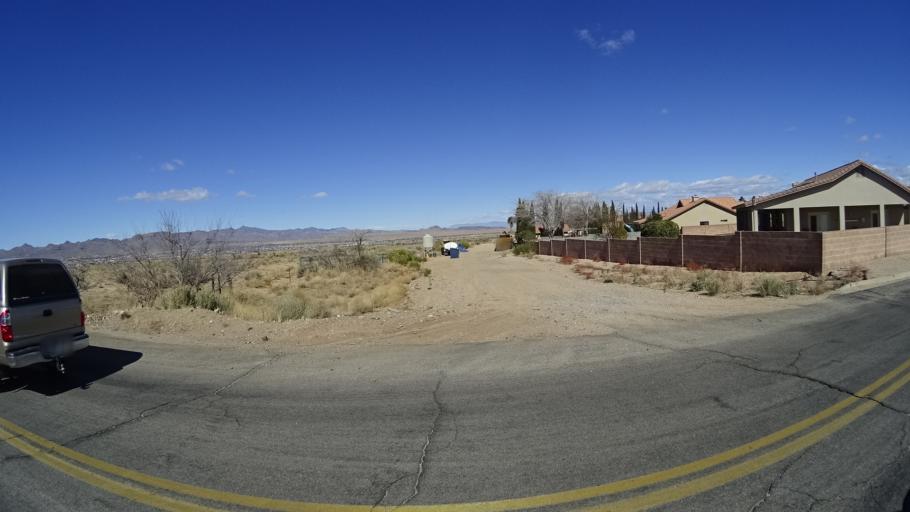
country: US
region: Arizona
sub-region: Mohave County
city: Kingman
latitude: 35.1958
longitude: -113.9761
